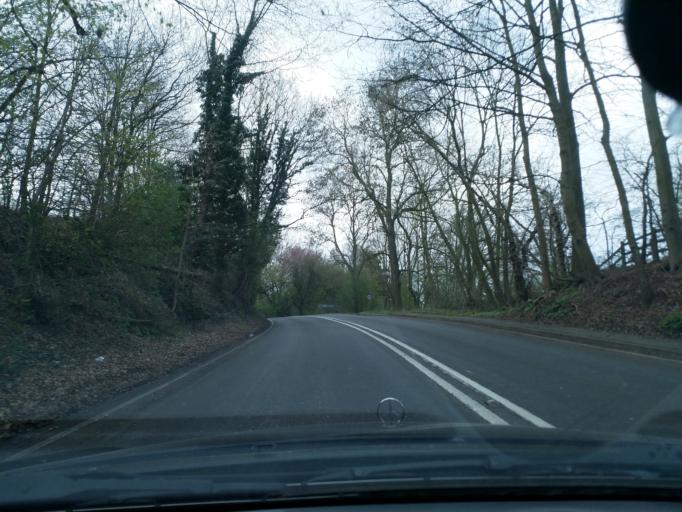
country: GB
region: England
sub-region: Warwickshire
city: Royal Leamington Spa
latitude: 52.3489
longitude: -1.5142
